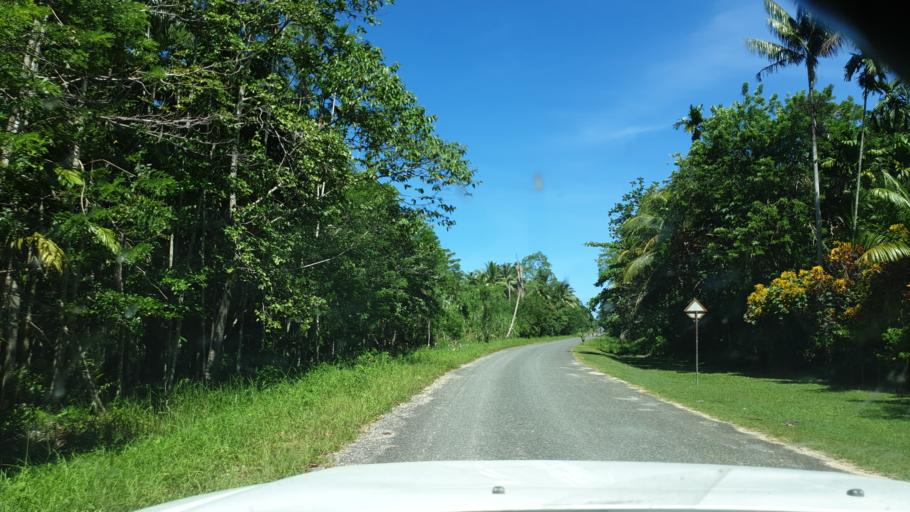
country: PG
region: Madang
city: Madang
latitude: -4.4458
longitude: 145.3561
